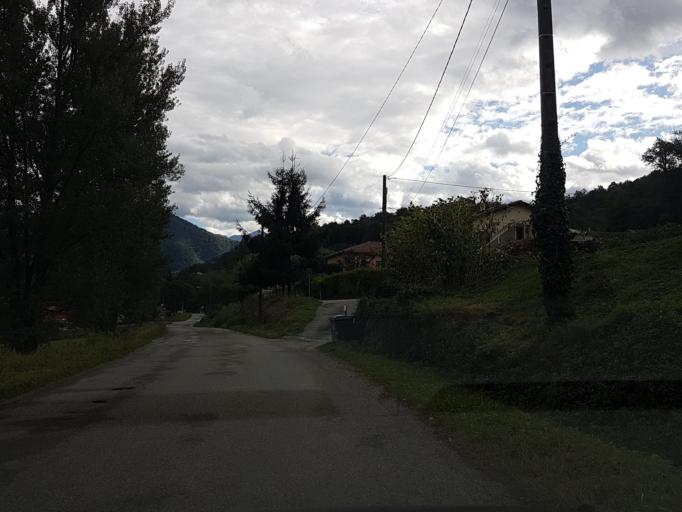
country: FR
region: Midi-Pyrenees
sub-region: Departement de l'Ariege
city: Saint-Girons
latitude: 42.8912
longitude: 1.2108
